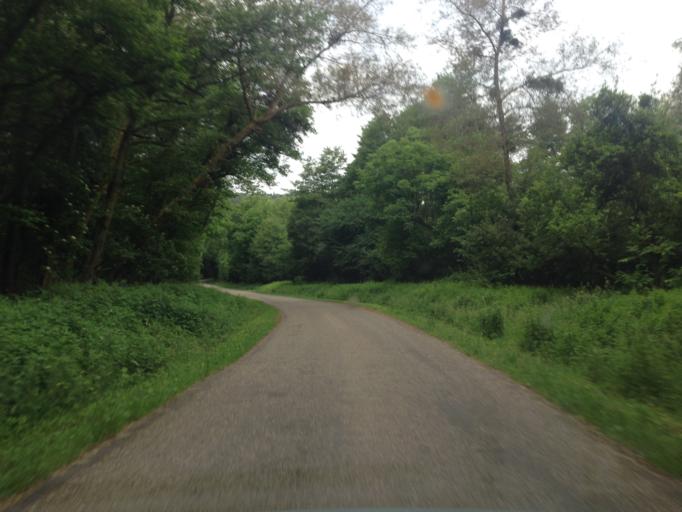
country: FR
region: Alsace
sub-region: Departement du Bas-Rhin
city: Neuwiller-les-Saverne
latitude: 48.8310
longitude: 7.3994
